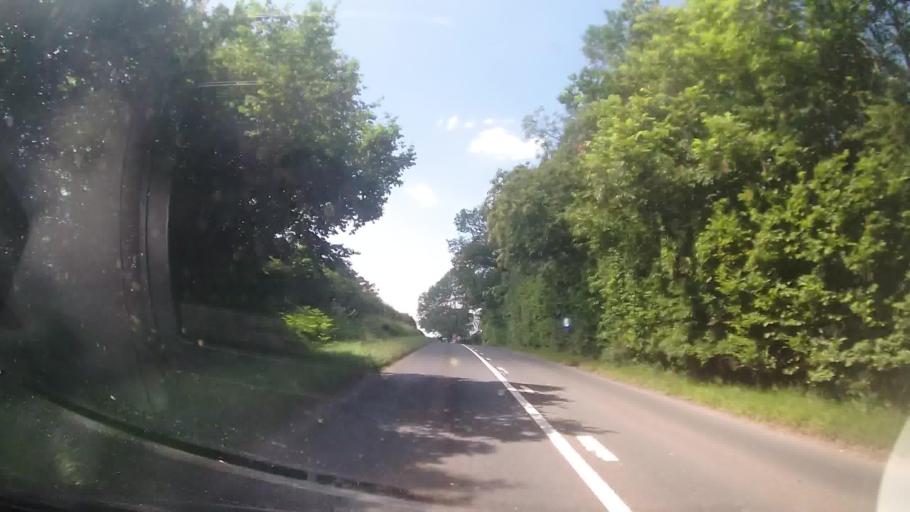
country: GB
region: England
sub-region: Herefordshire
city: Yatton
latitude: 52.0569
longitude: -2.5284
